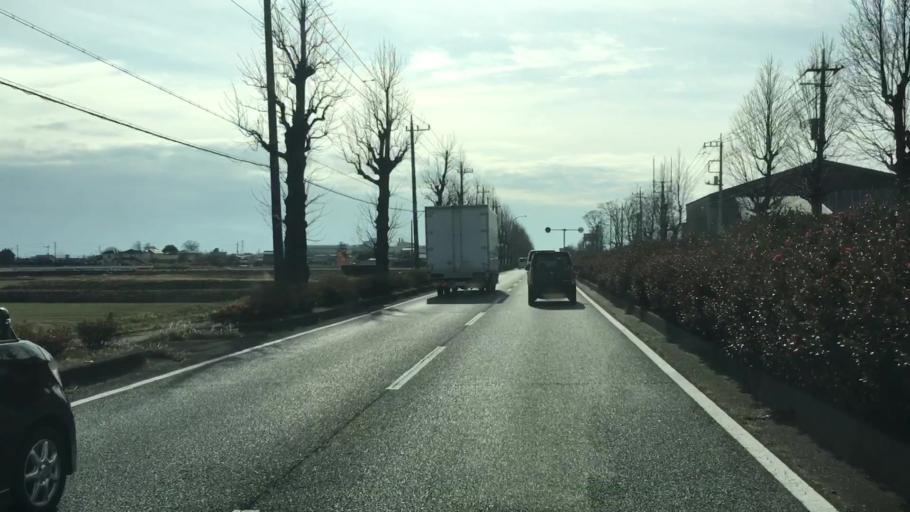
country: JP
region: Saitama
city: Menuma
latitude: 36.1970
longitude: 139.3705
